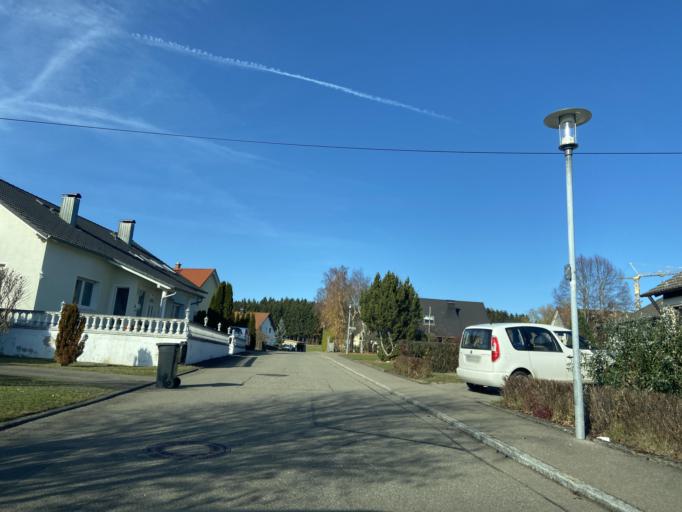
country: DE
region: Baden-Wuerttemberg
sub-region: Tuebingen Region
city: Schwenningen
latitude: 48.1156
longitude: 9.0278
